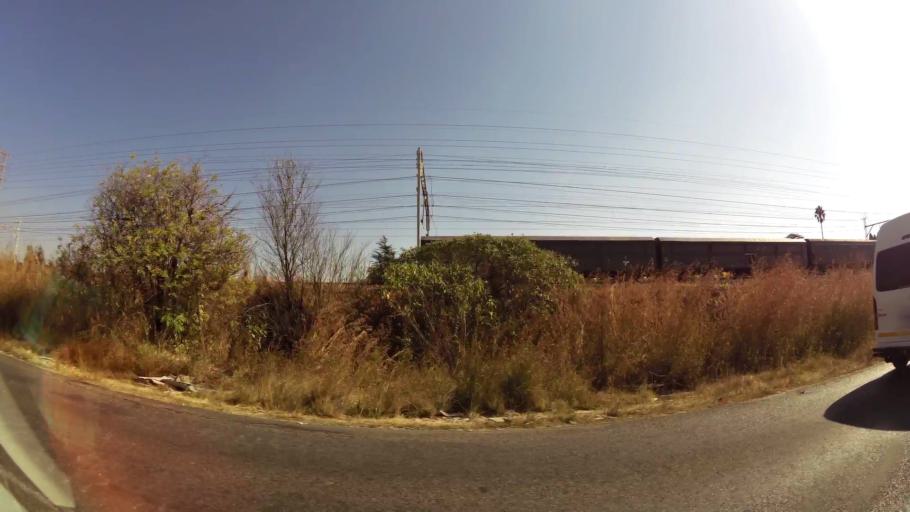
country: ZA
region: Gauteng
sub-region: Ekurhuleni Metropolitan Municipality
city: Tembisa
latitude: -26.0564
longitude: 28.2448
